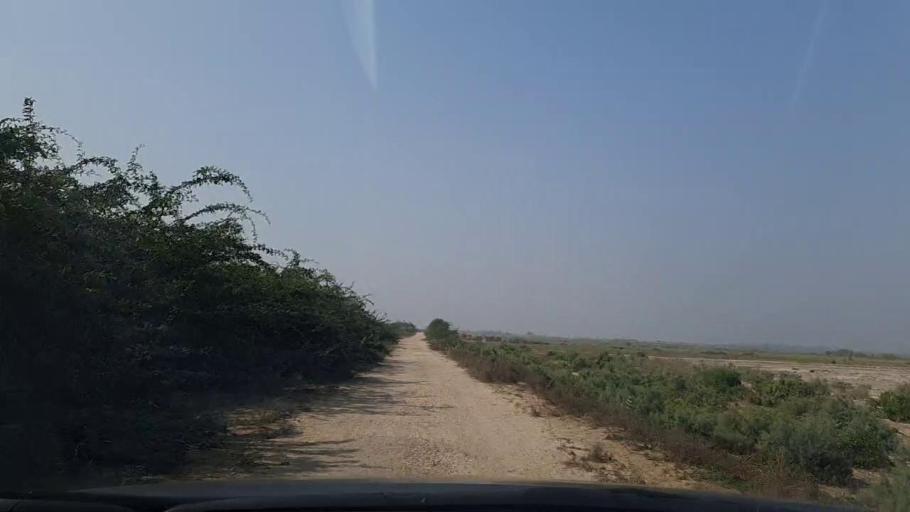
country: PK
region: Sindh
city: Mirpur Sakro
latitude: 24.5750
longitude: 67.7670
